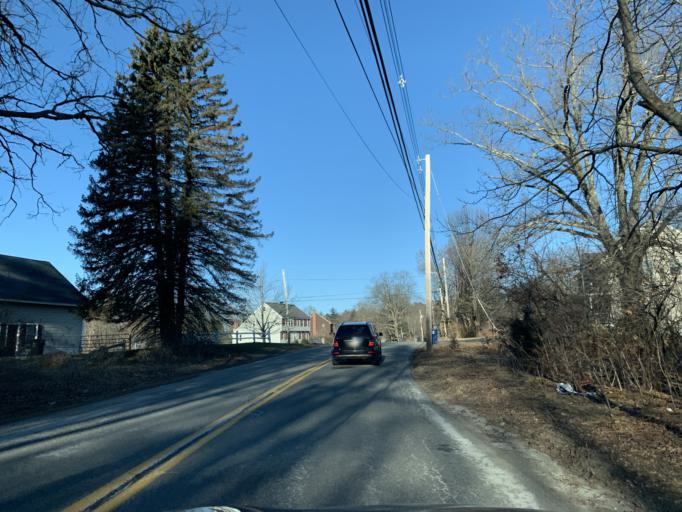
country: US
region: Massachusetts
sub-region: Middlesex County
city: Dracut
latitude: 42.7101
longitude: -71.2587
